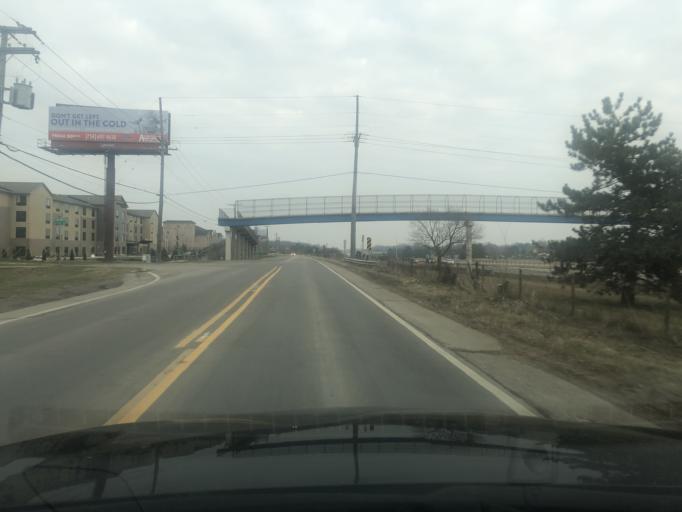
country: US
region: Michigan
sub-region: Wayne County
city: Belleville
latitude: 42.2200
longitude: -83.4949
